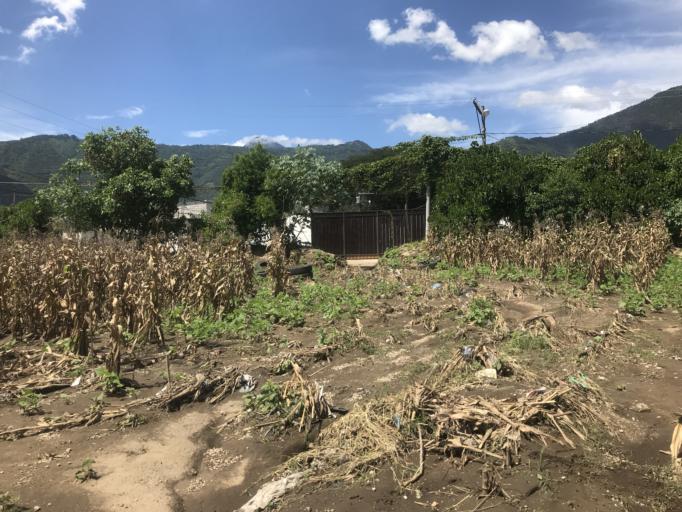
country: GT
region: Guatemala
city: Amatitlan
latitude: 14.4801
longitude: -90.6327
